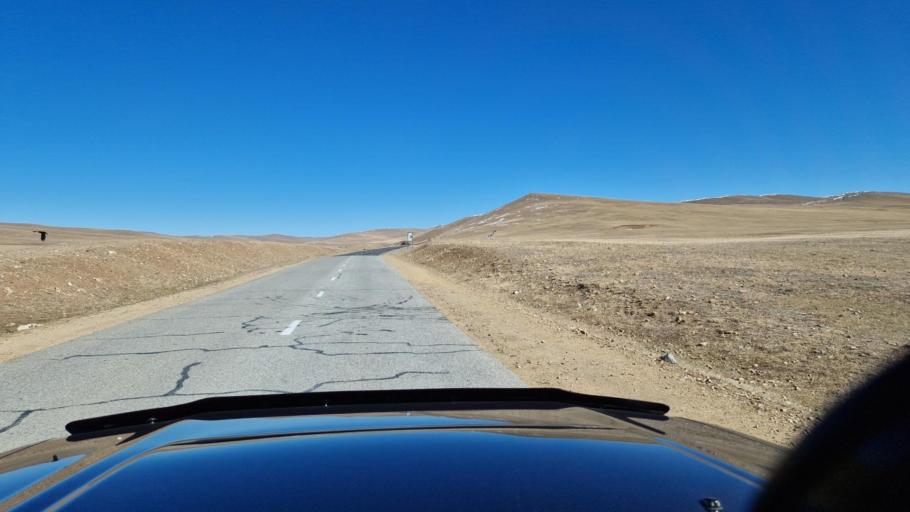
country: MN
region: Hentiy
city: Modot
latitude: 47.7590
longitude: 108.6328
